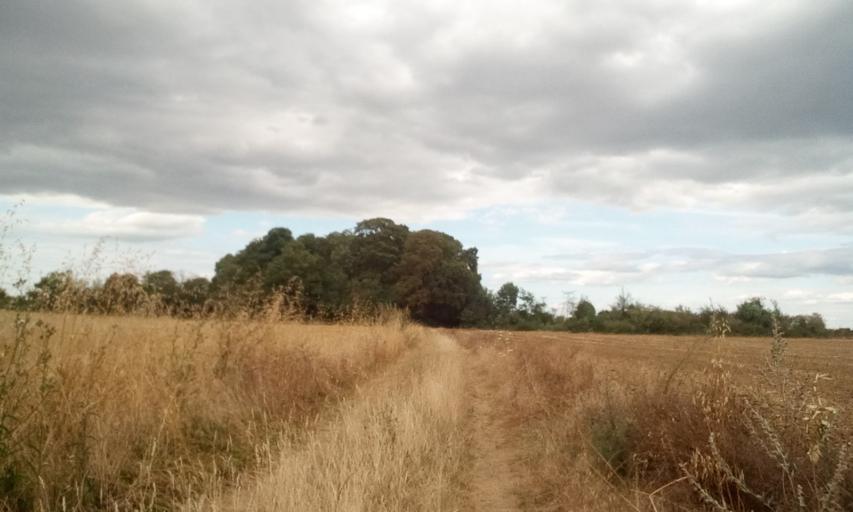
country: FR
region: Lower Normandy
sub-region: Departement du Calvados
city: Bellengreville
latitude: 49.1261
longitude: -0.2229
